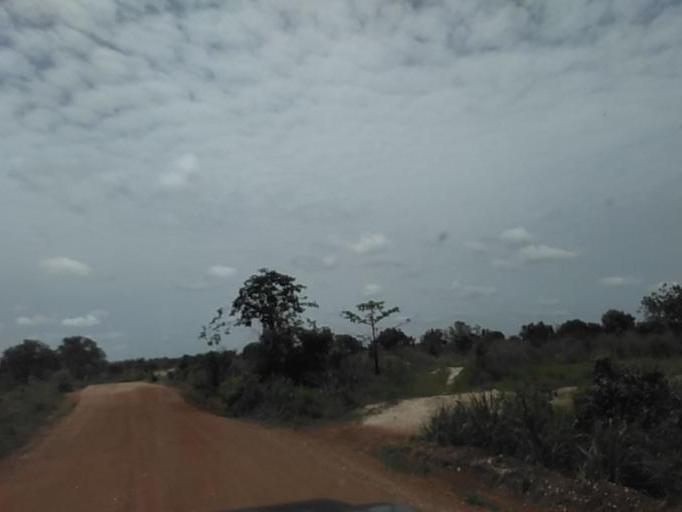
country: GH
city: Akropong
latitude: 6.0963
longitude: 0.2556
